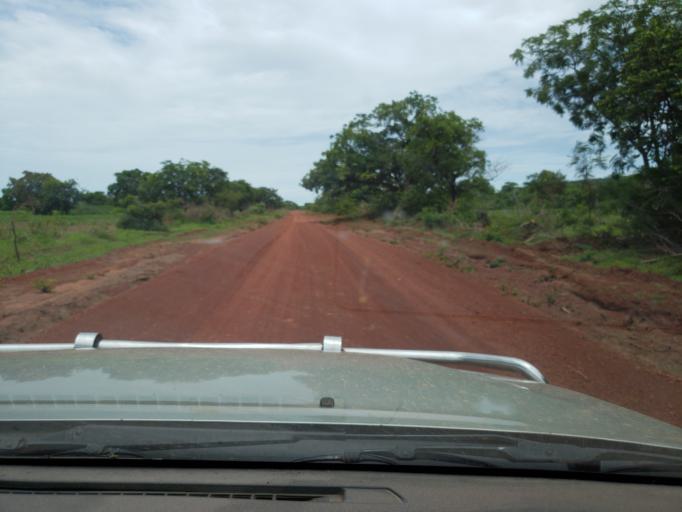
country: ML
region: Sikasso
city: Sikasso
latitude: 11.6574
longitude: -6.3421
